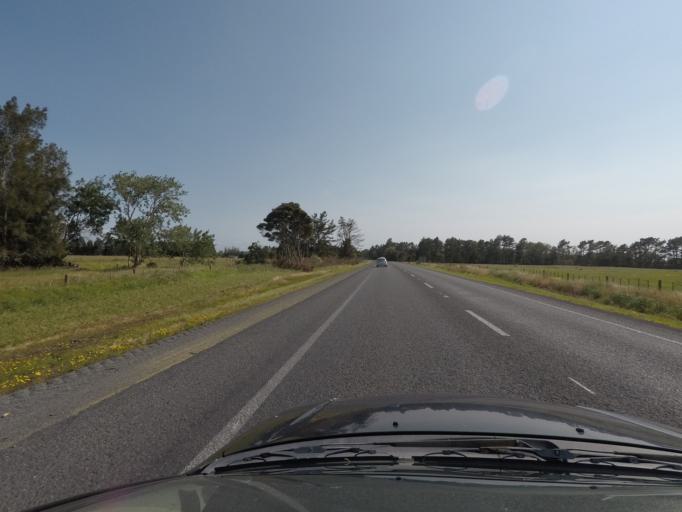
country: NZ
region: Northland
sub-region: Whangarei
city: Ruakaka
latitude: -35.9619
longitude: 174.4477
